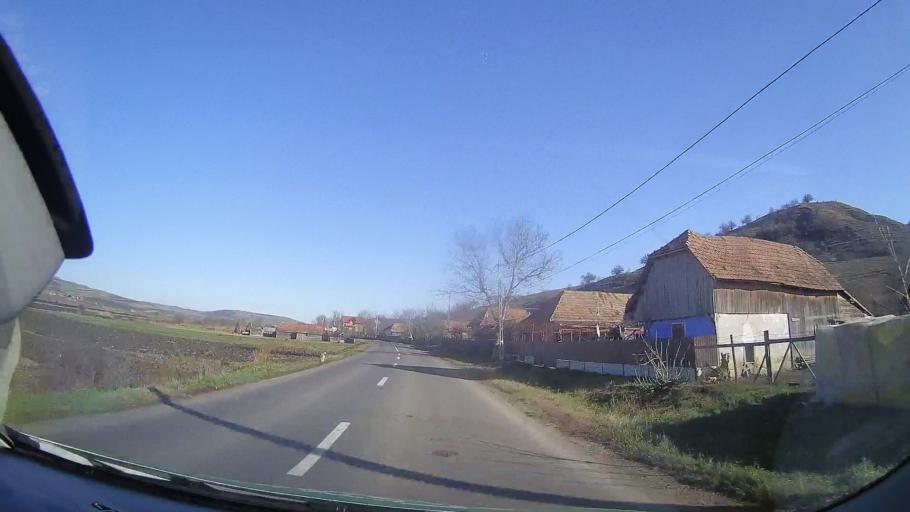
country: RO
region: Mures
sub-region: Comuna Band
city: Band
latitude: 46.5635
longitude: 24.3387
